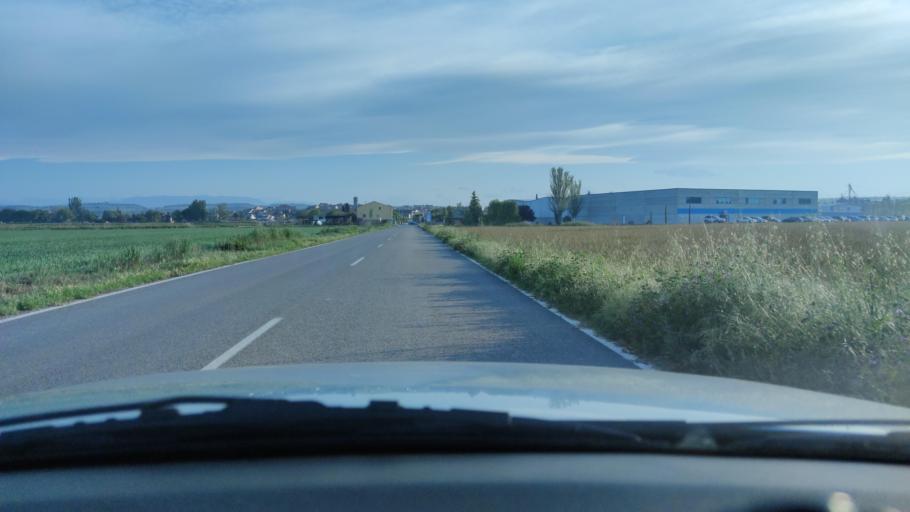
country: ES
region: Catalonia
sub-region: Provincia de Lleida
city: Castellsera
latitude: 41.7391
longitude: 0.9853
